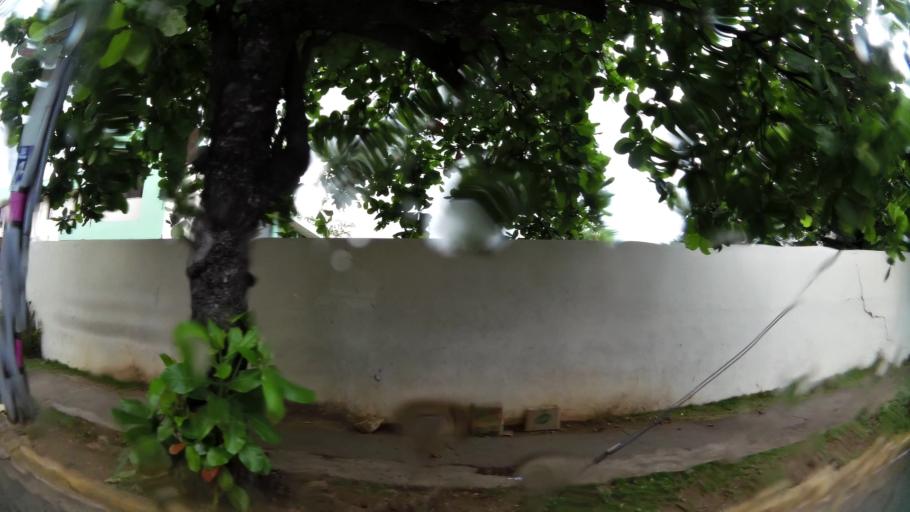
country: DO
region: Nacional
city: Ciudad Nueva
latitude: 18.4719
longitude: -69.9126
